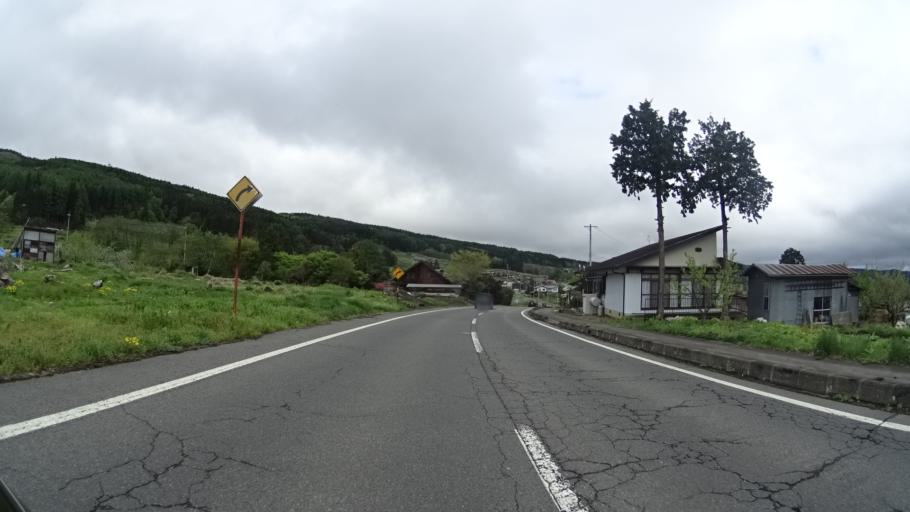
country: JP
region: Nagano
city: Nagano-shi
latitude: 36.7353
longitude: 138.2061
